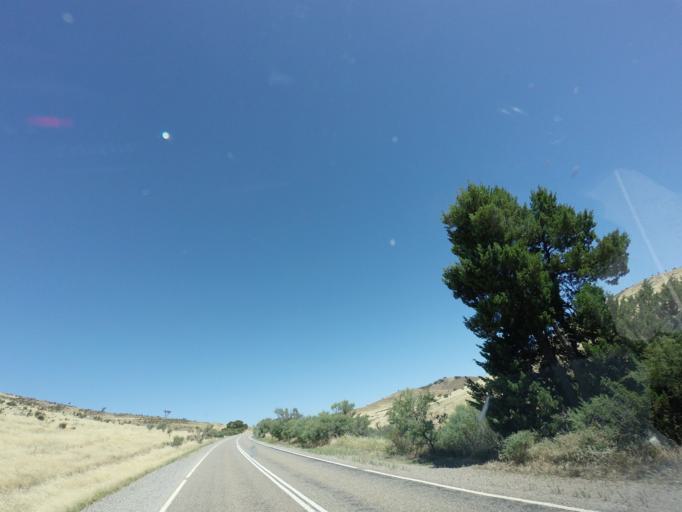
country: AU
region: South Australia
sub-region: Peterborough
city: Peterborough
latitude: -32.7354
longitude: 138.5410
